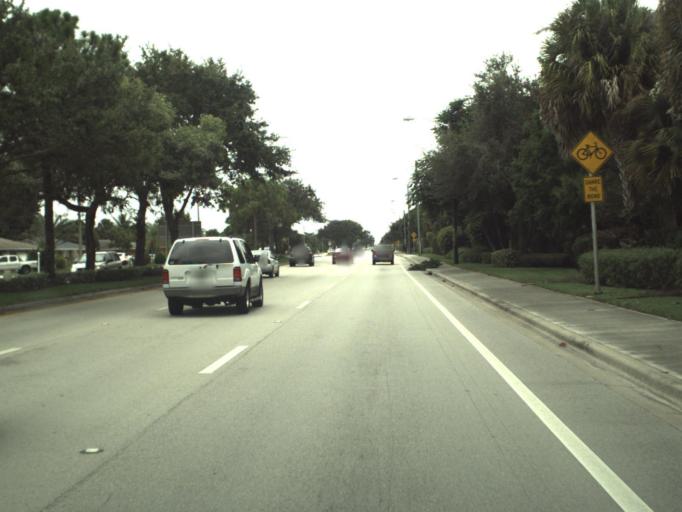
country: US
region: Florida
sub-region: Palm Beach County
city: North Palm Beach
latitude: 26.8171
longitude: -80.1062
